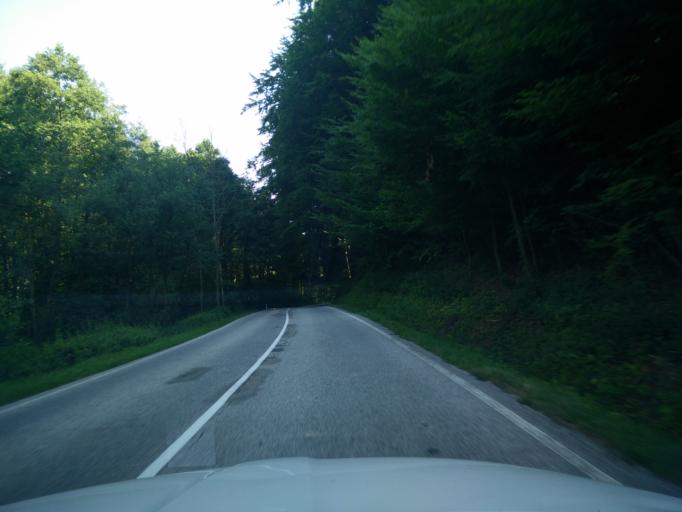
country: SK
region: Nitriansky
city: Bojnice
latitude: 48.8615
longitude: 18.4609
